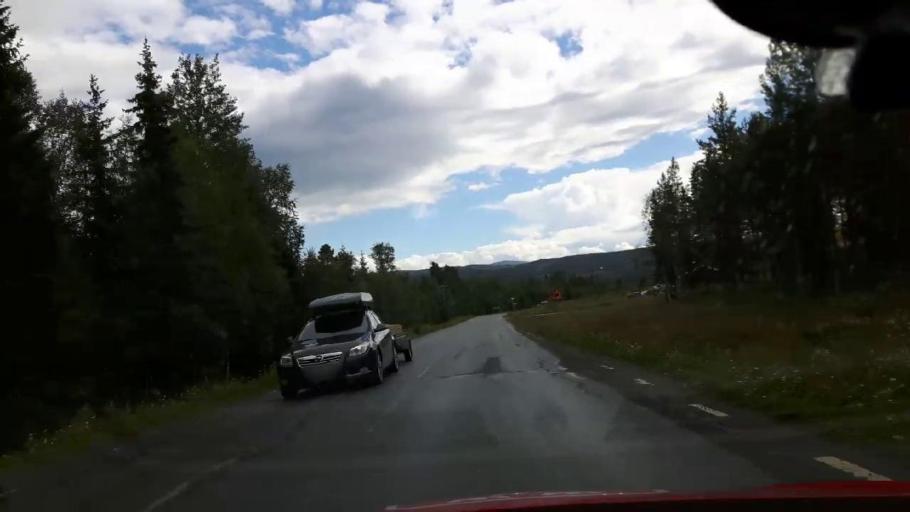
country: SE
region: Jaemtland
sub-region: Are Kommun
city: Are
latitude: 63.3223
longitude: 13.2324
